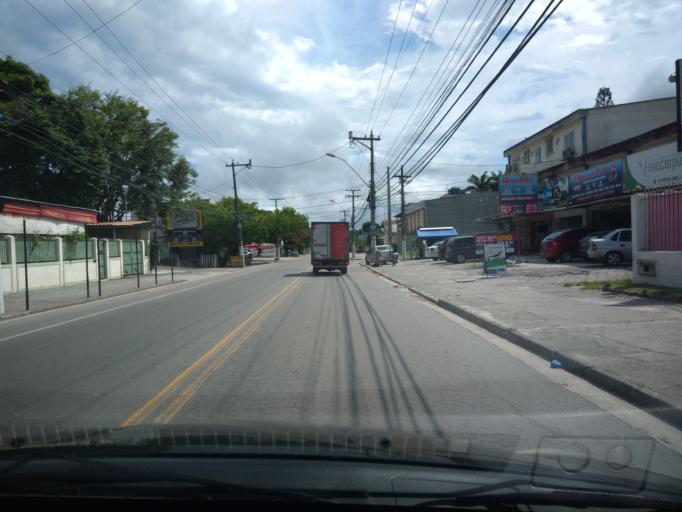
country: BR
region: Rio de Janeiro
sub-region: Niteroi
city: Niteroi
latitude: -22.9342
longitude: -43.0218
